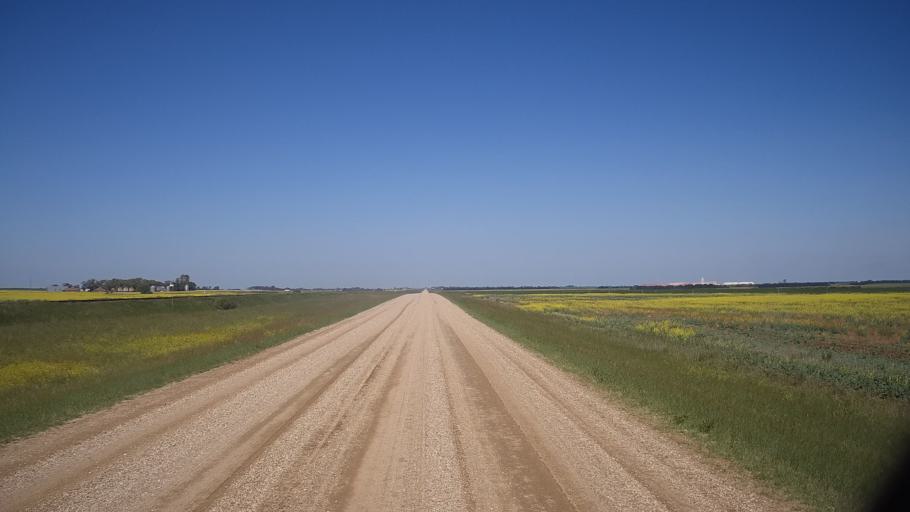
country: CA
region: Saskatchewan
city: Watrous
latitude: 51.8658
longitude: -105.9788
